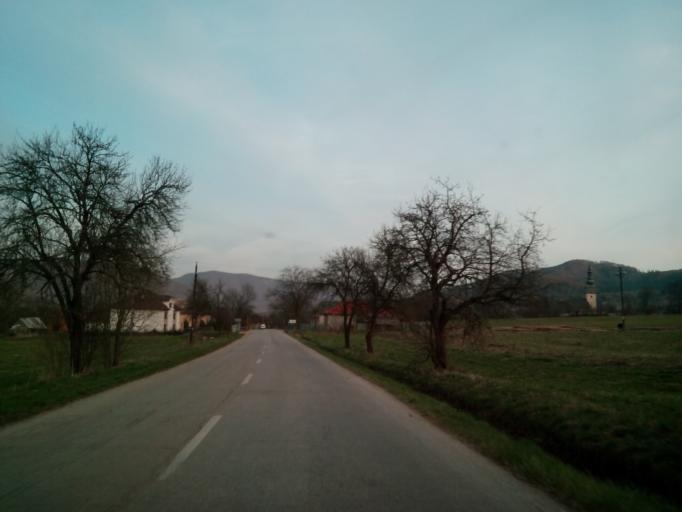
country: SK
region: Kosicky
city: Dobsina
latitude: 48.6874
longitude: 20.3228
